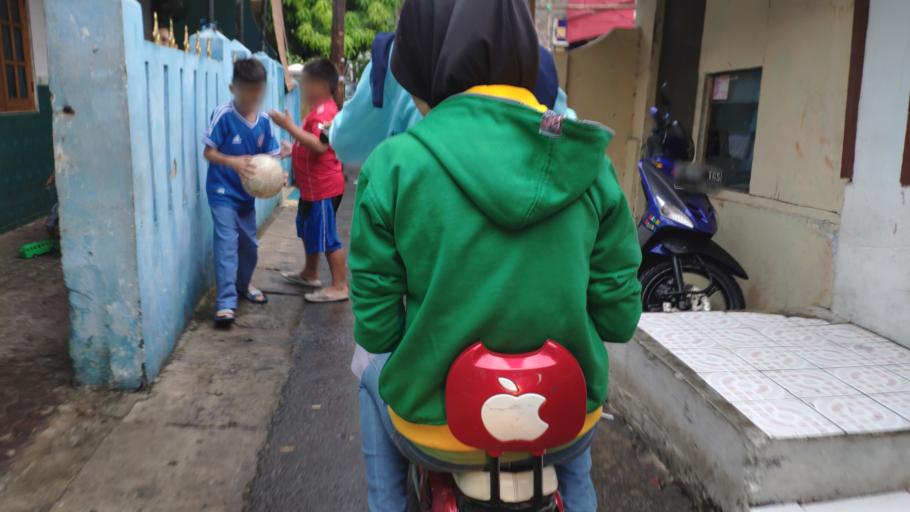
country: ID
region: Jakarta Raya
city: Jakarta
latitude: -6.2074
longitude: 106.8727
